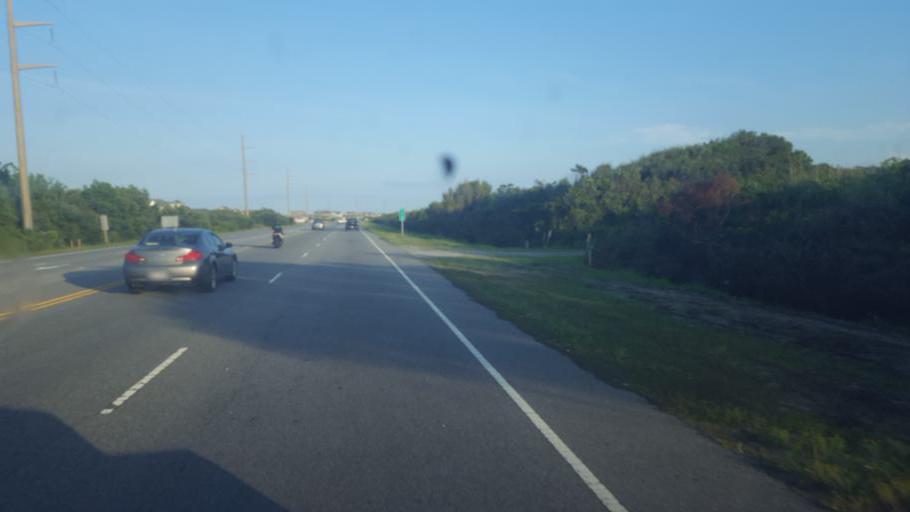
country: US
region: North Carolina
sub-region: Dare County
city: Nags Head
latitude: 35.9667
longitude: -75.6319
